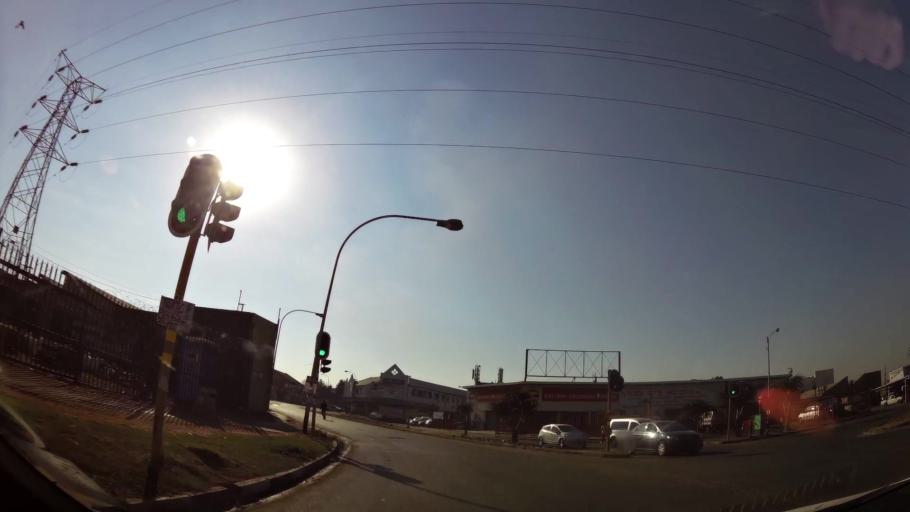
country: ZA
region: Gauteng
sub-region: Ekurhuleni Metropolitan Municipality
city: Germiston
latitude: -26.2008
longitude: 28.1200
